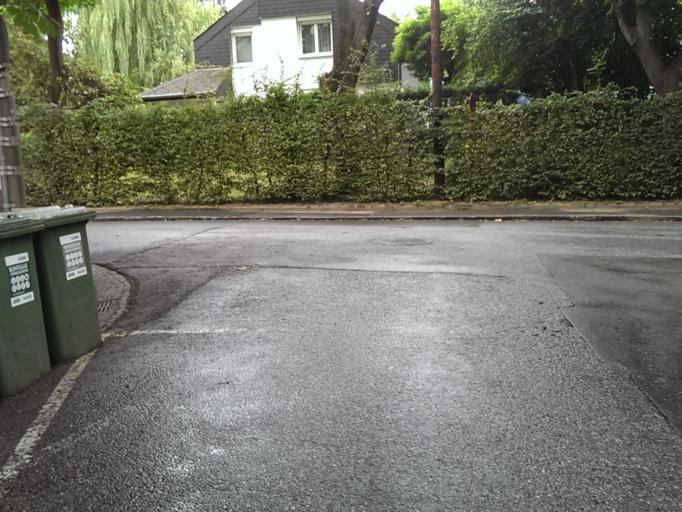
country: AT
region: Styria
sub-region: Graz Stadt
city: Graz
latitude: 47.0649
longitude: 15.4690
